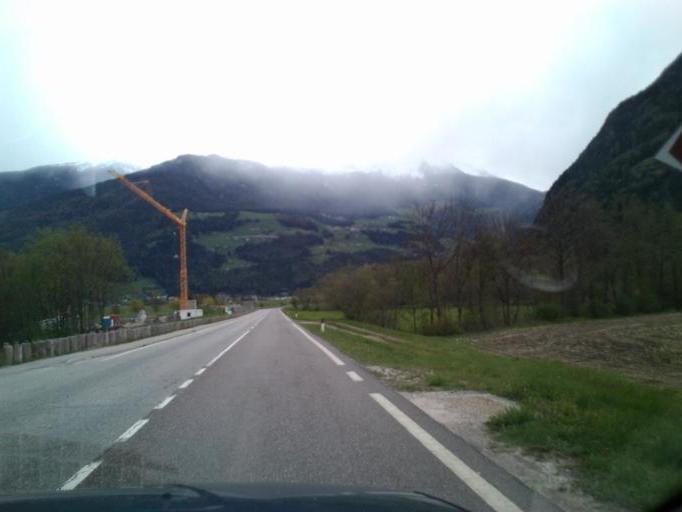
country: IT
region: Trentino-Alto Adige
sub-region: Bolzano
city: Molini di Tures
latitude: 46.8972
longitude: 11.9470
